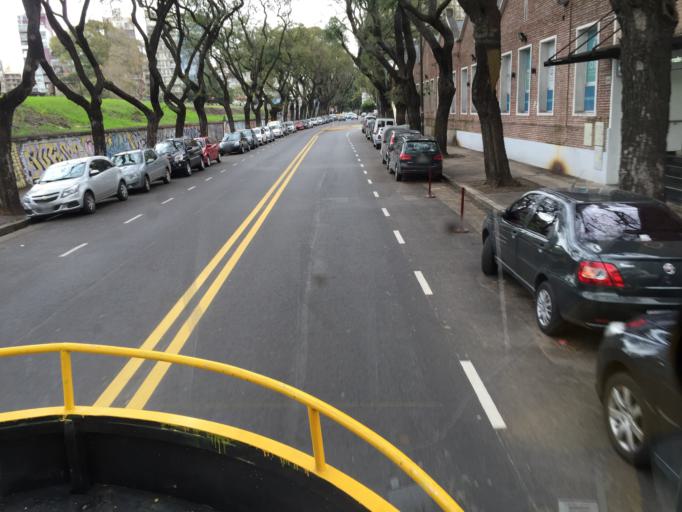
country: AR
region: Buenos Aires F.D.
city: Colegiales
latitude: -34.5737
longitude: -58.4291
